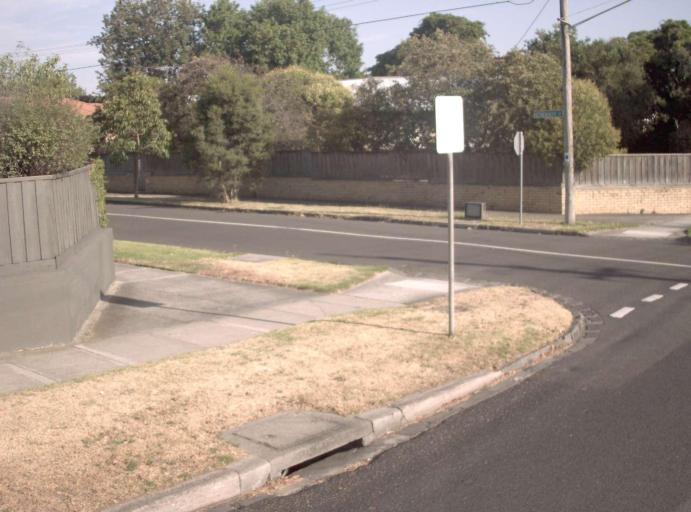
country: AU
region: Victoria
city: Murrumbeena
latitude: -37.8955
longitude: 145.0654
